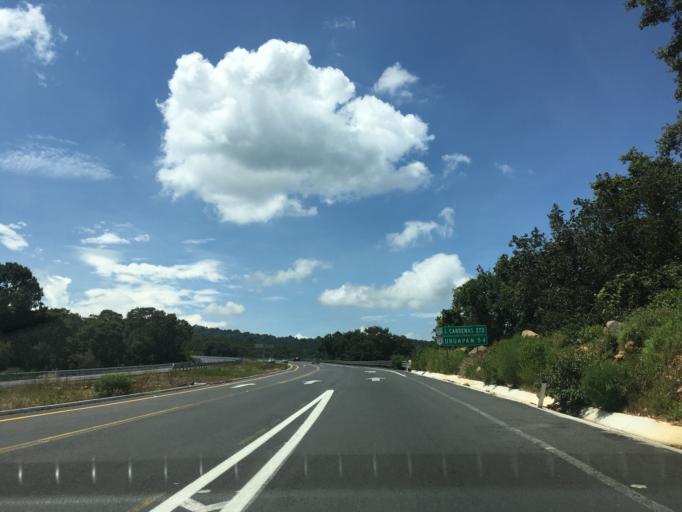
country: MX
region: Michoacan
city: Patzcuaro
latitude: 19.5246
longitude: -101.5701
